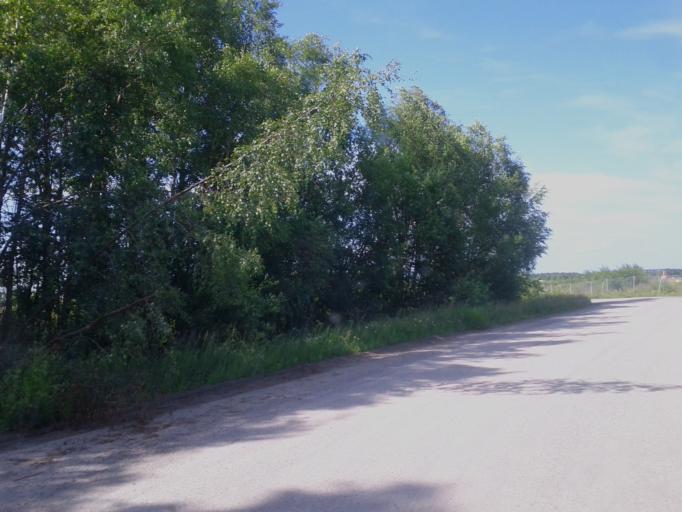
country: SE
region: Vaesterbotten
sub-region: Umea Kommun
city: Umea
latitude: 63.7794
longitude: 20.2999
